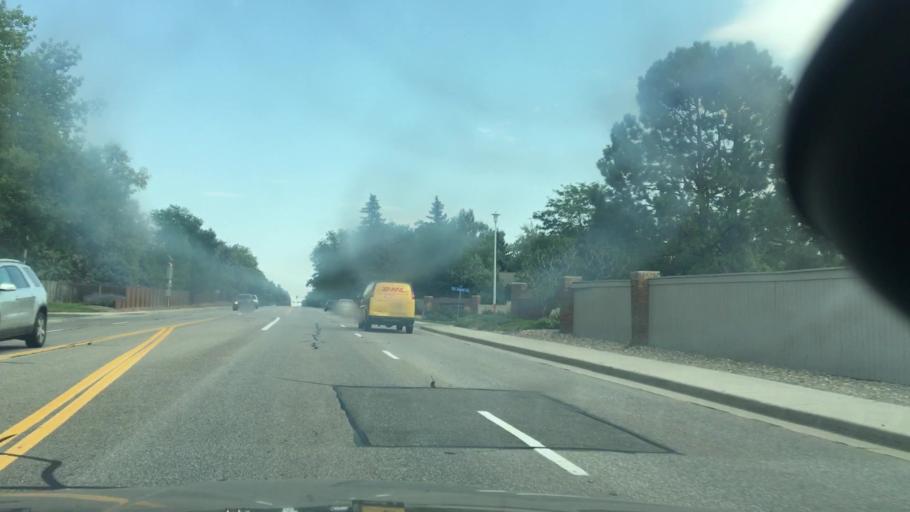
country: US
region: Colorado
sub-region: Arapahoe County
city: Castlewood
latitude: 39.5805
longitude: -104.8974
